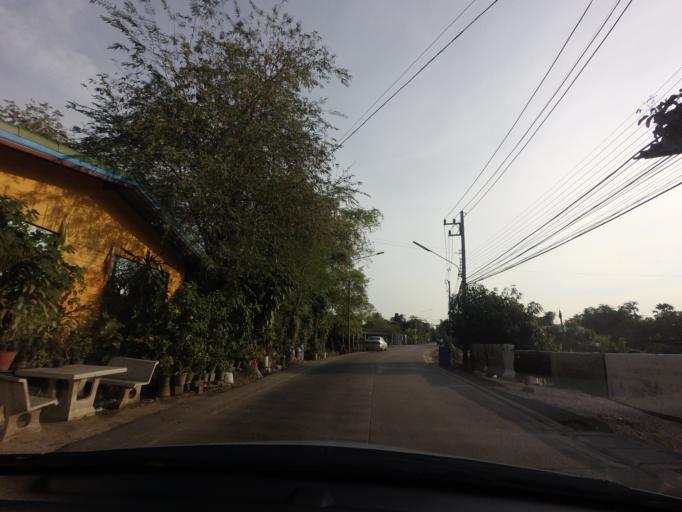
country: TH
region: Pathum Thani
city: Pathum Thani
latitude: 14.0403
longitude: 100.5507
